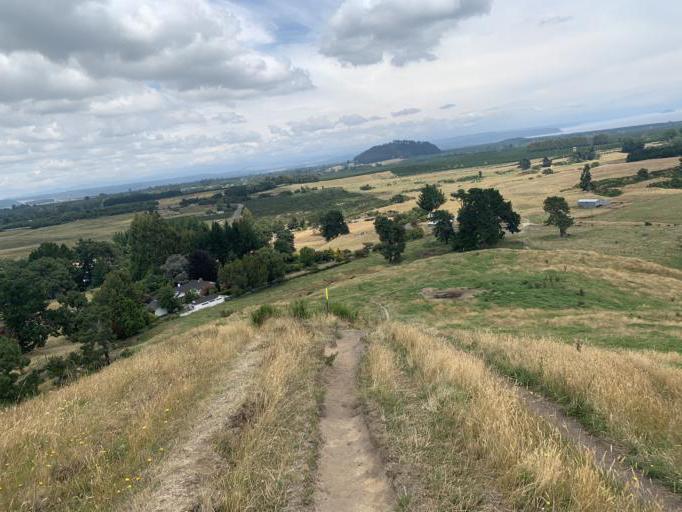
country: NZ
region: Waikato
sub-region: Taupo District
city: Taupo
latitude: -38.7018
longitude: 176.1422
